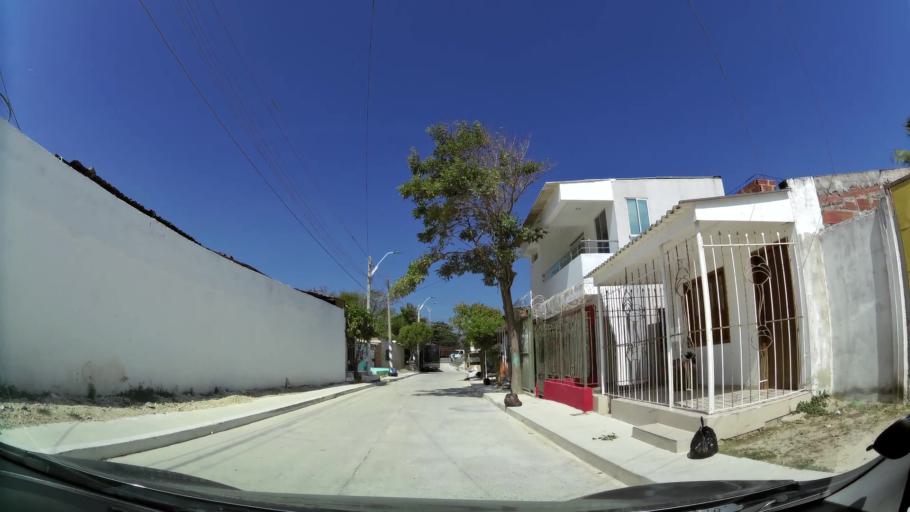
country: CO
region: Atlantico
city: Barranquilla
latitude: 10.9702
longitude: -74.8368
